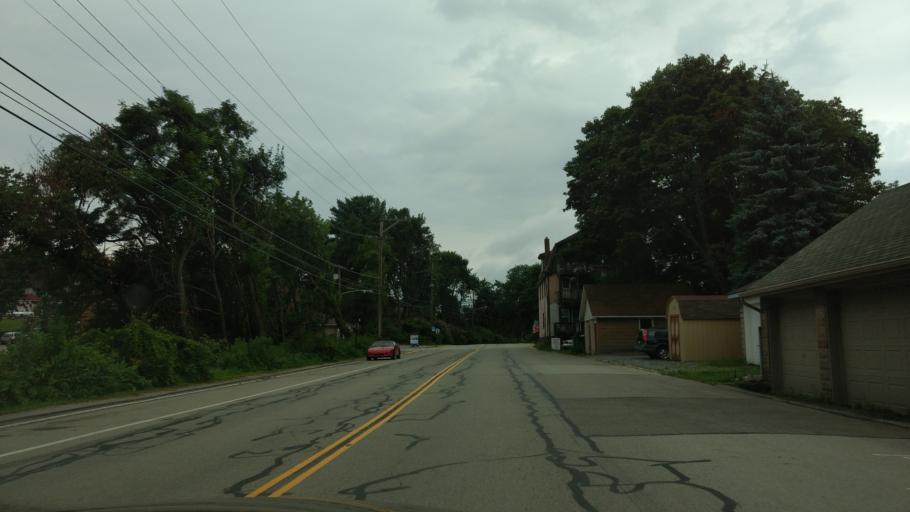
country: US
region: Pennsylvania
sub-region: Allegheny County
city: West View
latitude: 40.5175
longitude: -80.0443
